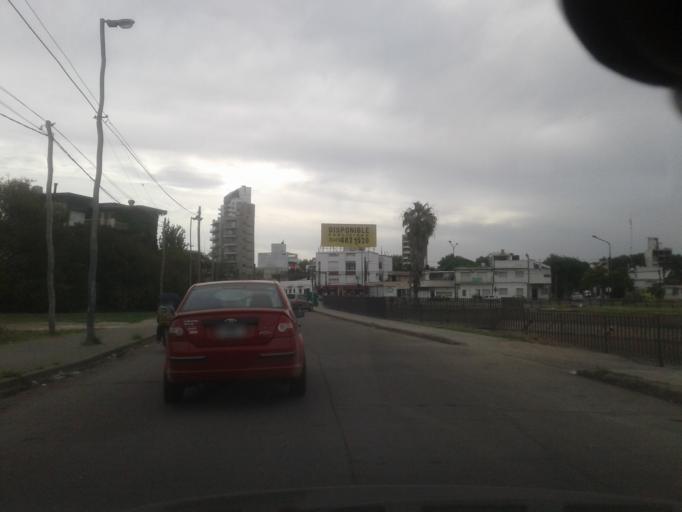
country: AR
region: Santa Fe
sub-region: Departamento de Rosario
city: Rosario
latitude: -32.9122
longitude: -60.6830
